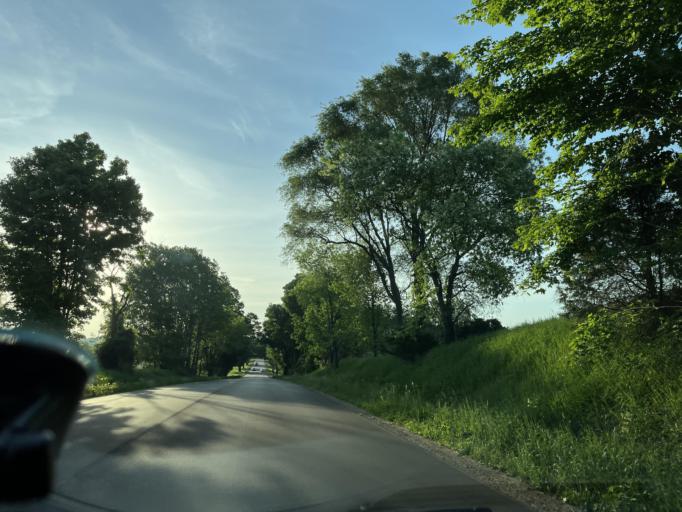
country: US
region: Michigan
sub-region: Barry County
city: Middleville
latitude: 42.7111
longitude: -85.4341
